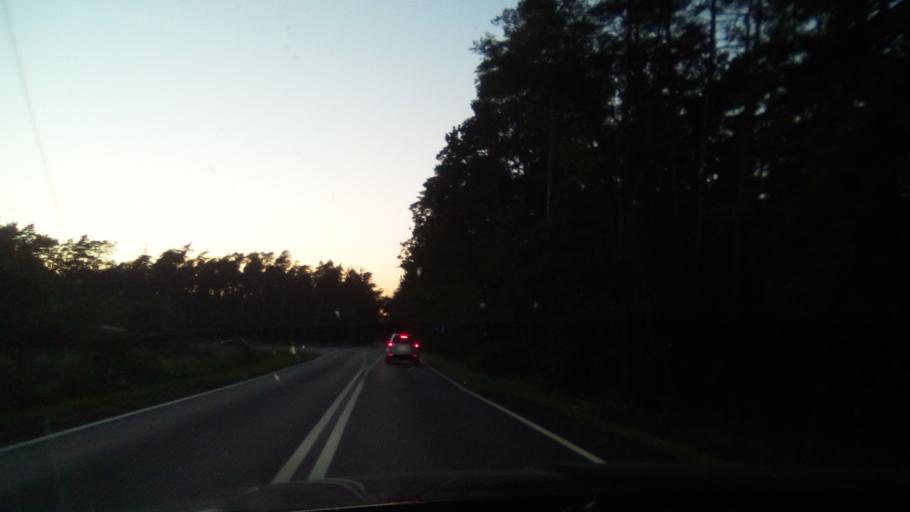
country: PL
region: West Pomeranian Voivodeship
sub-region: Powiat goleniowski
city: Goleniow
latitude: 53.5727
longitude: 14.7921
